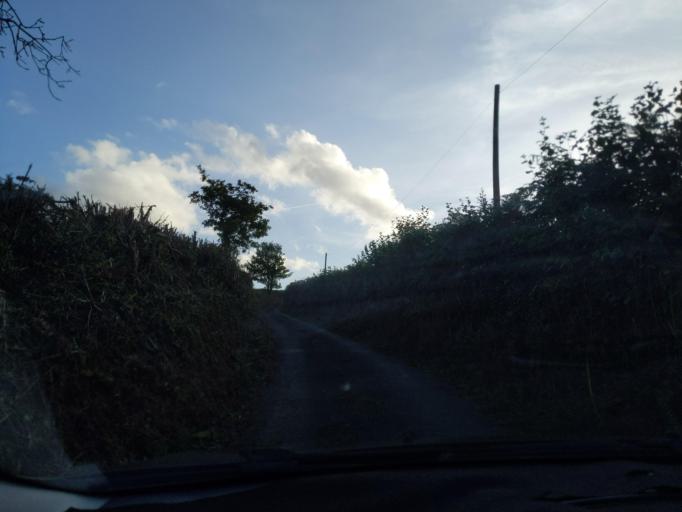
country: GB
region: England
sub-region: Devon
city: Bovey Tracey
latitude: 50.6328
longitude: -3.6699
